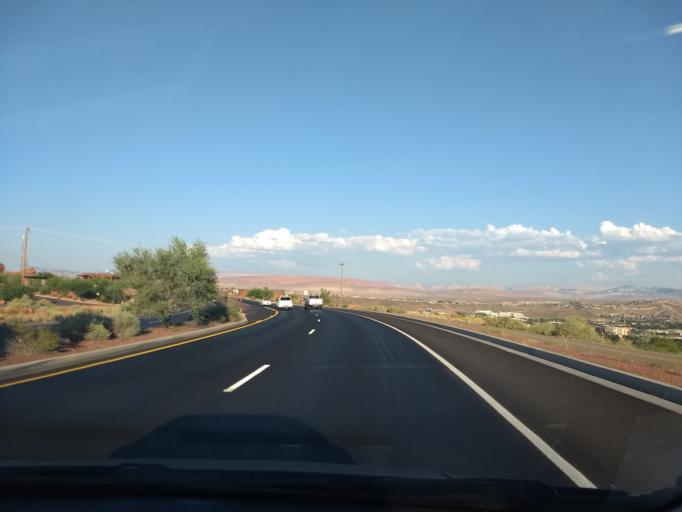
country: US
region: Utah
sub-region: Washington County
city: Saint George
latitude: 37.1138
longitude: -113.5771
